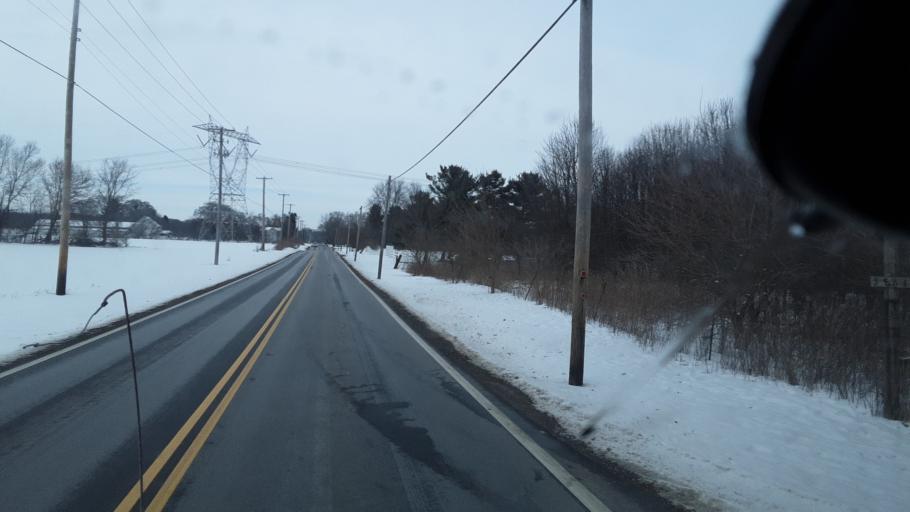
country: US
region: Ohio
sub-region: Delaware County
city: Powell
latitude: 40.2282
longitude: -83.1509
